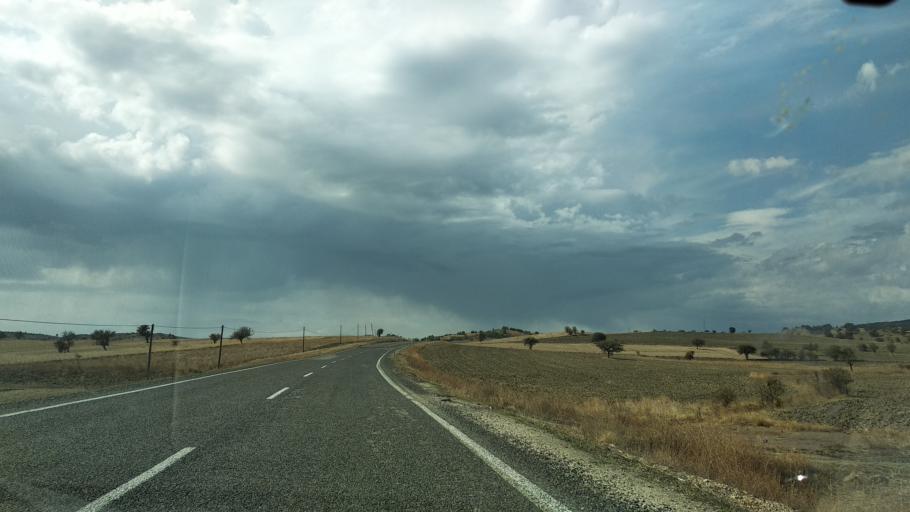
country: TR
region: Bolu
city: Seben
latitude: 40.3900
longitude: 31.5443
